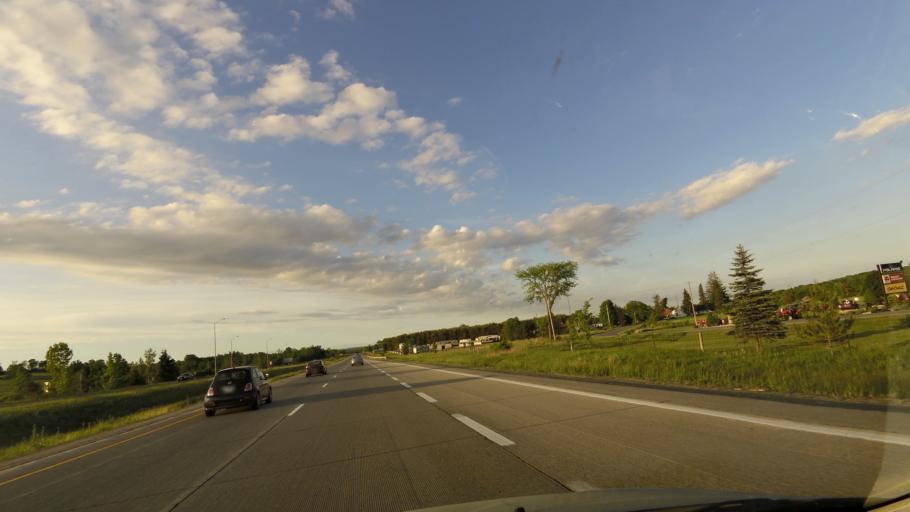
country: CA
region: Ontario
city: Omemee
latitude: 44.1868
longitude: -78.4618
